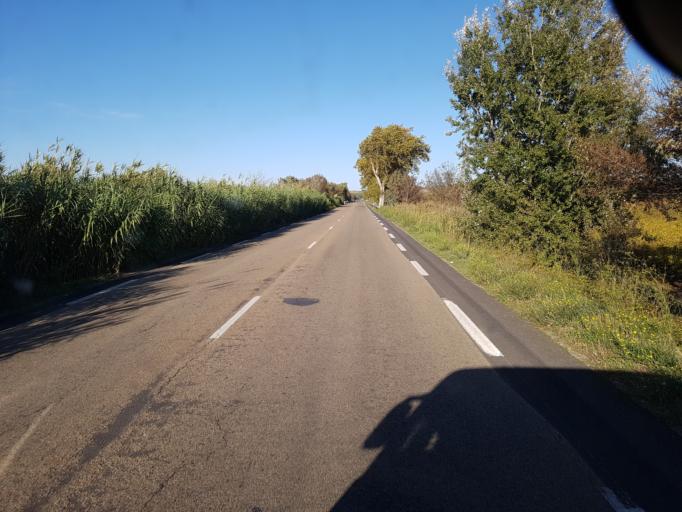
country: FR
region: Languedoc-Roussillon
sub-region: Departement de l'Aude
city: Coursan
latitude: 43.2505
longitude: 3.0689
